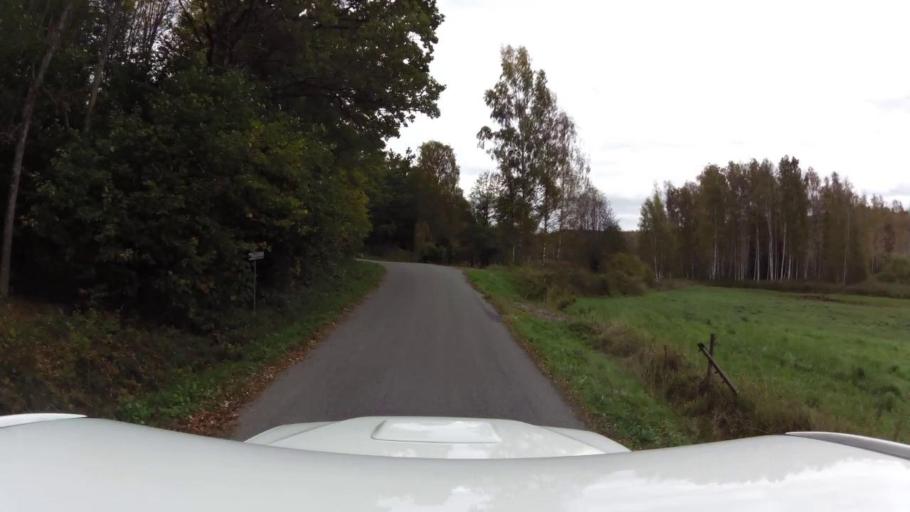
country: SE
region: OEstergoetland
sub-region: Kinda Kommun
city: Rimforsa
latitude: 58.2006
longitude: 15.5604
